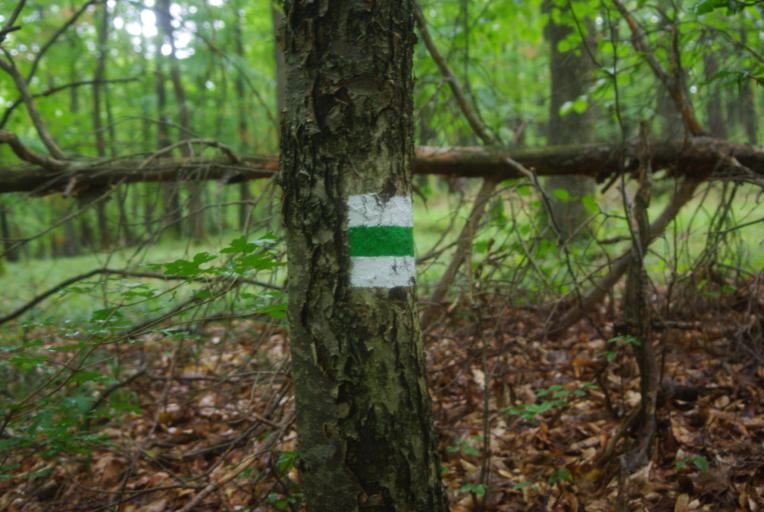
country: HU
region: Borsod-Abauj-Zemplen
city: Gonc
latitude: 48.3957
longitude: 21.3615
